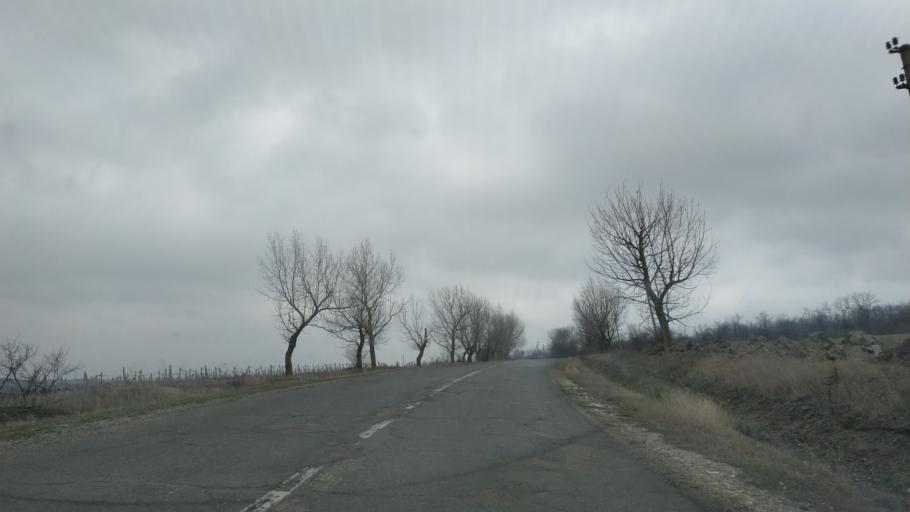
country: MD
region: Gagauzia
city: Bugeac
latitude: 46.3523
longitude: 28.7901
